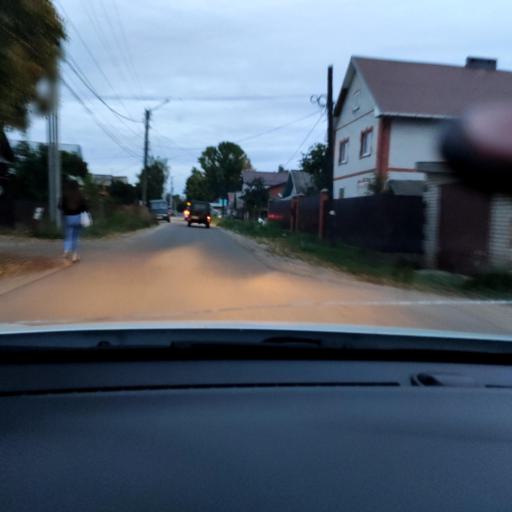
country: RU
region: Mariy-El
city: Volzhsk
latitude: 55.8683
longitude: 48.3632
